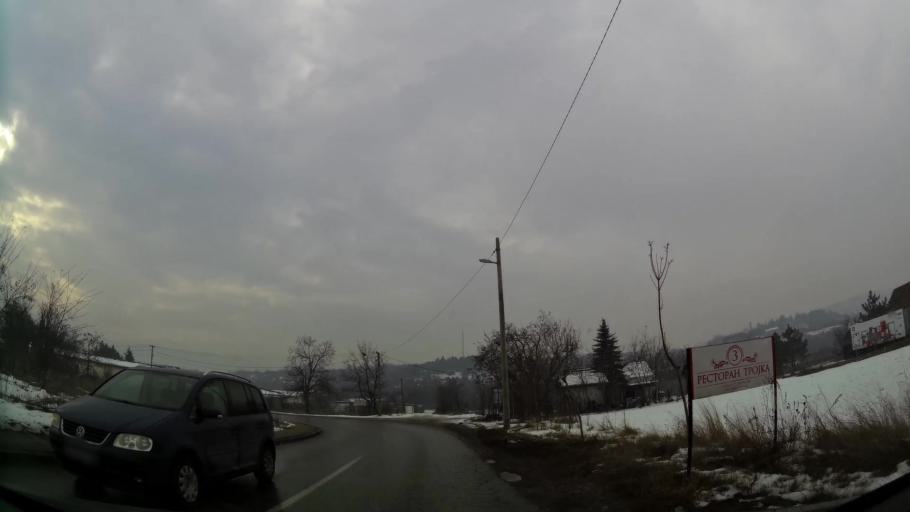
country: MK
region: Saraj
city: Saraj
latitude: 42.0239
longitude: 21.3490
